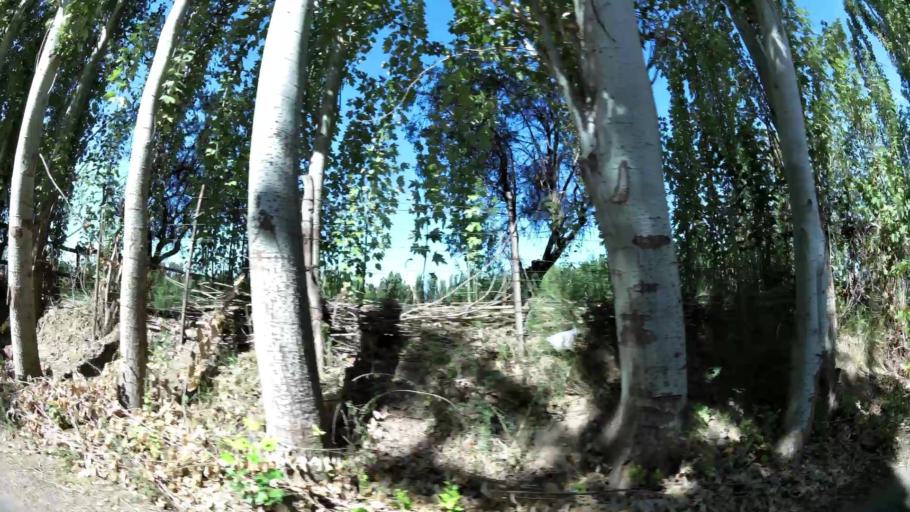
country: AR
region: Mendoza
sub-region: Departamento de Godoy Cruz
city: Godoy Cruz
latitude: -32.9790
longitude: -68.8421
